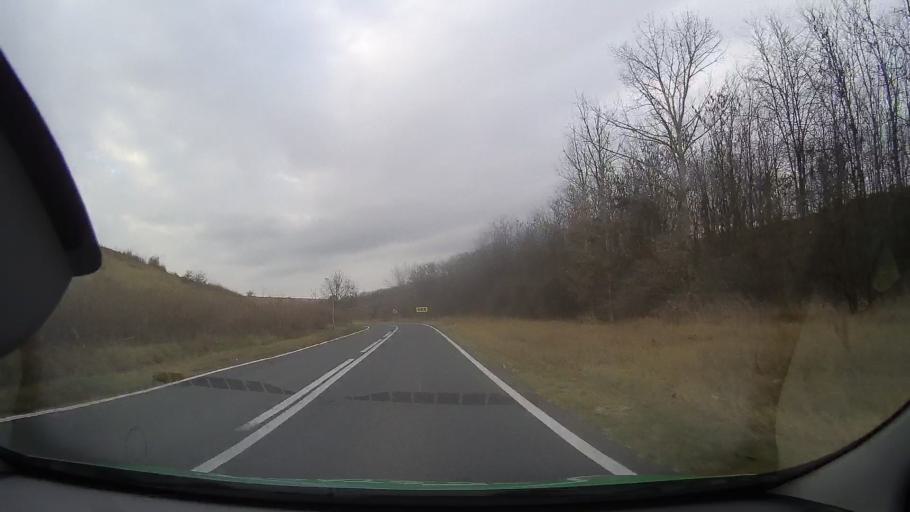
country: RO
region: Constanta
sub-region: Comuna Deleni
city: Deleni
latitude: 44.0999
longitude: 28.0296
